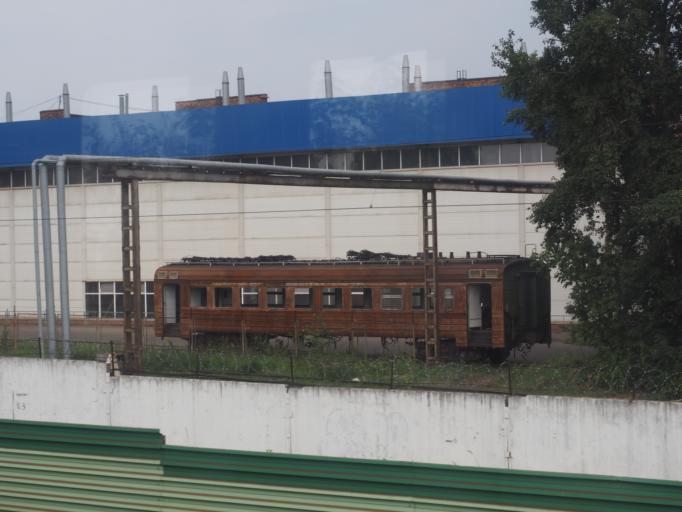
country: RU
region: Moscow
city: Ryazanskiy
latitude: 55.7406
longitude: 37.7465
